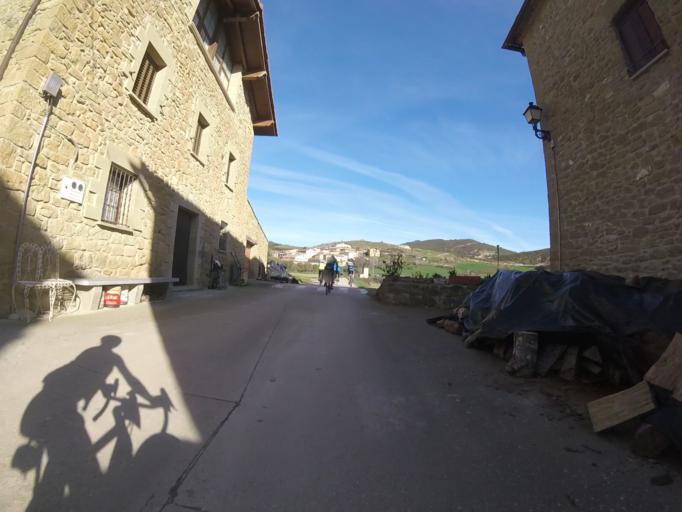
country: ES
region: Navarre
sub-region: Provincia de Navarra
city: Yerri
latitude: 42.6915
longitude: -1.9578
